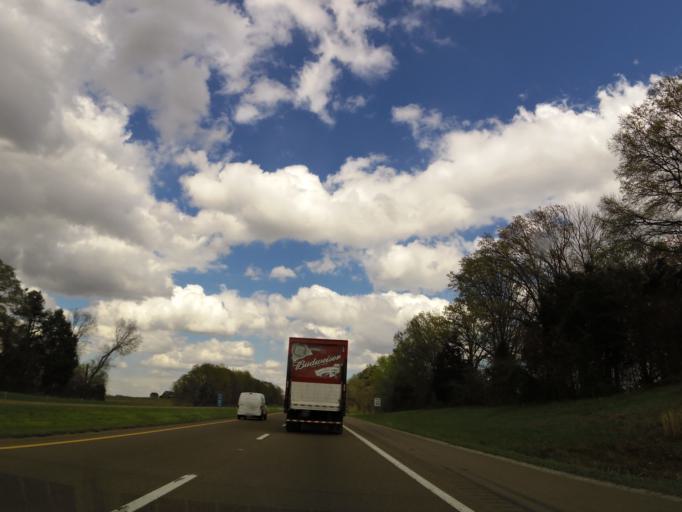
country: US
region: Tennessee
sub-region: Crockett County
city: Bells
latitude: 35.5993
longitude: -89.0486
